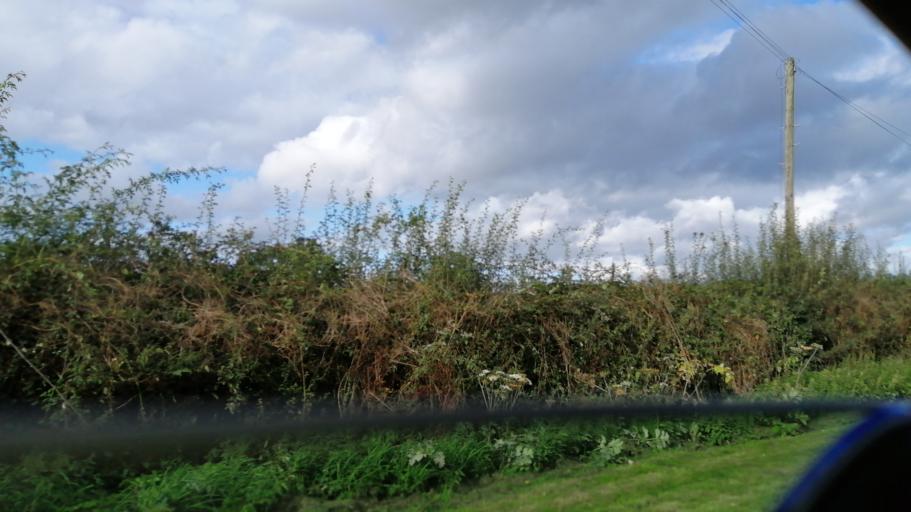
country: GB
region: England
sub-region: Herefordshire
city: Callow
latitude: 52.0097
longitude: -2.7515
